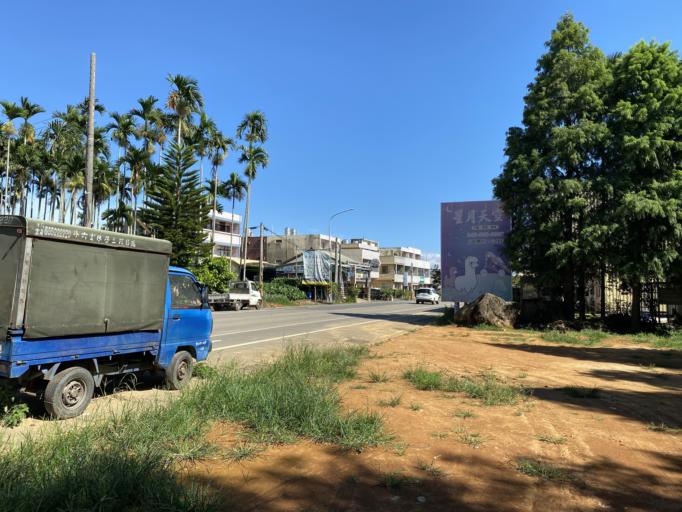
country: TW
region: Taiwan
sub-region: Nantou
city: Nantou
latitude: 23.9159
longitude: 120.6376
